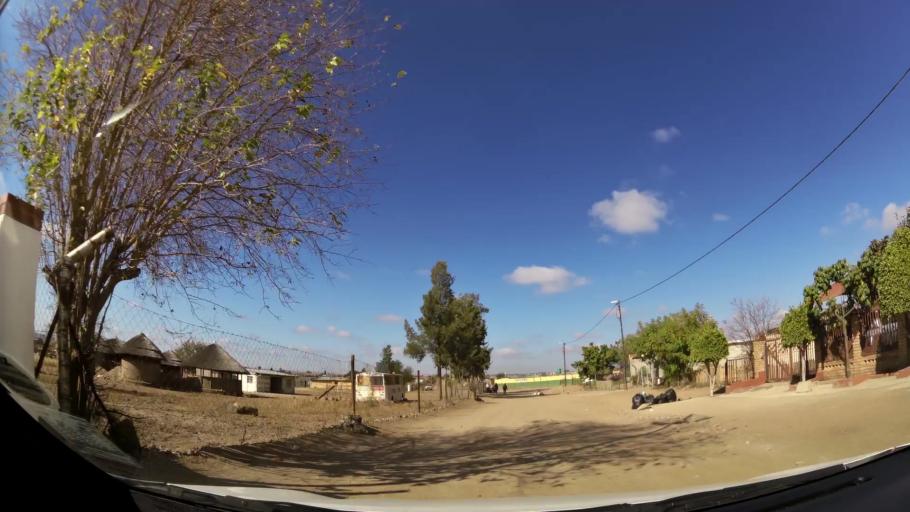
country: ZA
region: Limpopo
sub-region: Capricorn District Municipality
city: Polokwane
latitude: -23.8580
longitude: 29.3806
